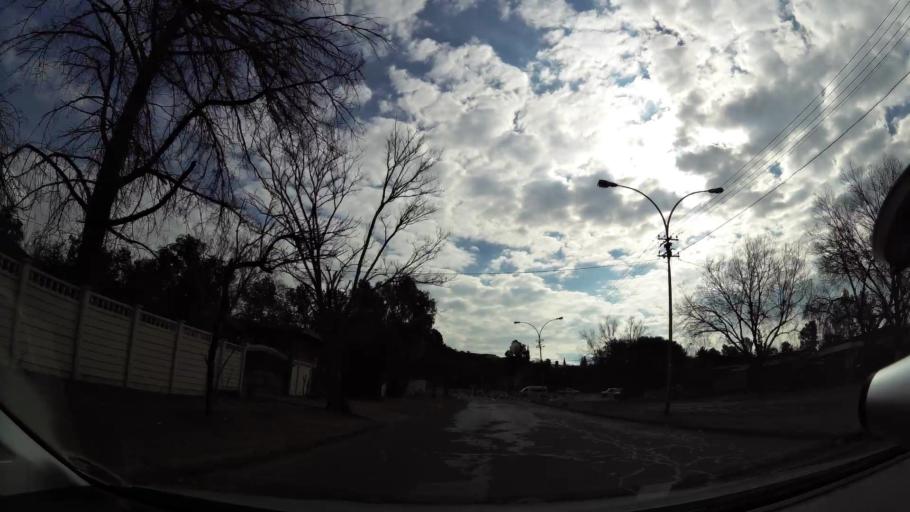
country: ZA
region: Orange Free State
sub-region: Mangaung Metropolitan Municipality
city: Bloemfontein
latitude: -29.0800
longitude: 26.2363
